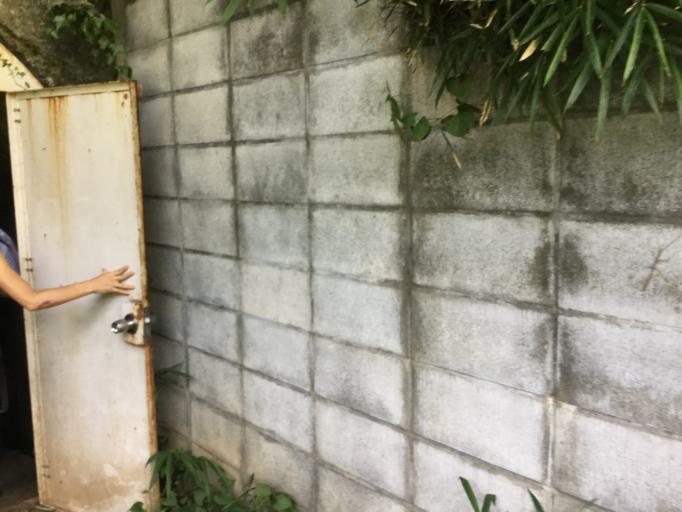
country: JP
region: Kanagawa
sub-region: Kawasaki-shi
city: Kawasaki
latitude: 35.5494
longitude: 139.6507
